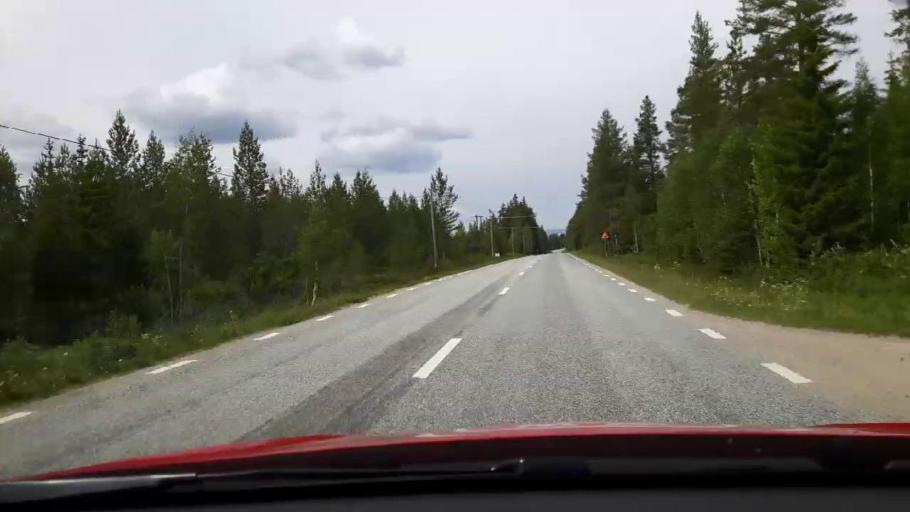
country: SE
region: Jaemtland
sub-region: Harjedalens Kommun
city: Sveg
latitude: 62.1500
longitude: 13.9045
